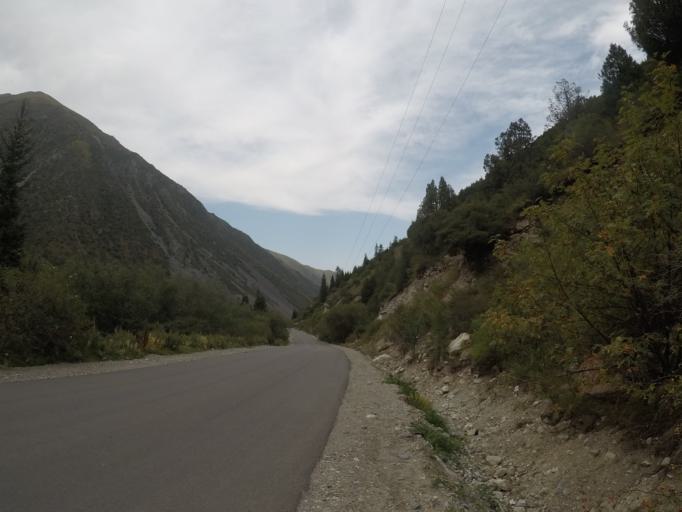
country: KG
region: Chuy
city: Bishkek
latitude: 42.5735
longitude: 74.4830
